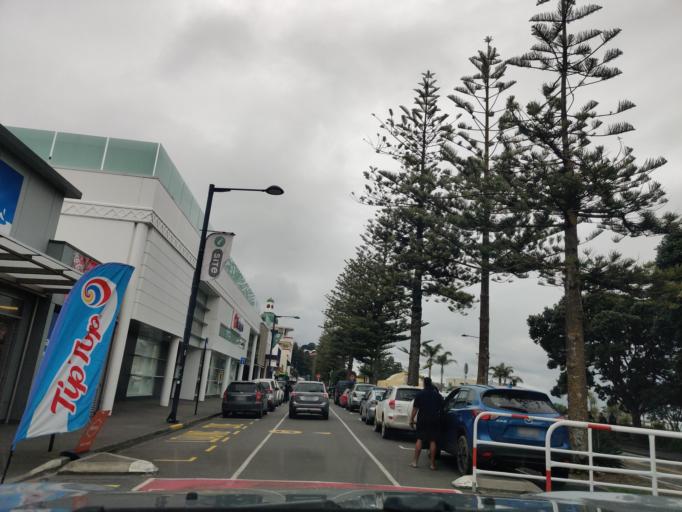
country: NZ
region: Hawke's Bay
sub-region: Napier City
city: Napier
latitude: -39.4915
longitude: 176.9192
